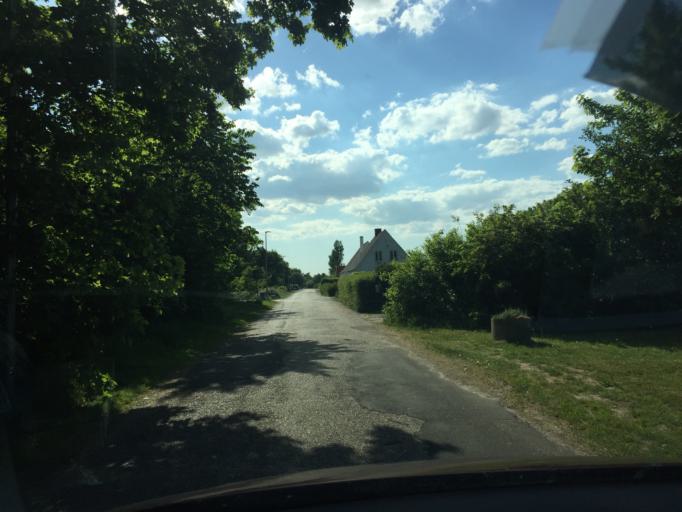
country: DE
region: Schleswig-Holstein
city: Aventoft
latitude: 54.9453
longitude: 8.8006
